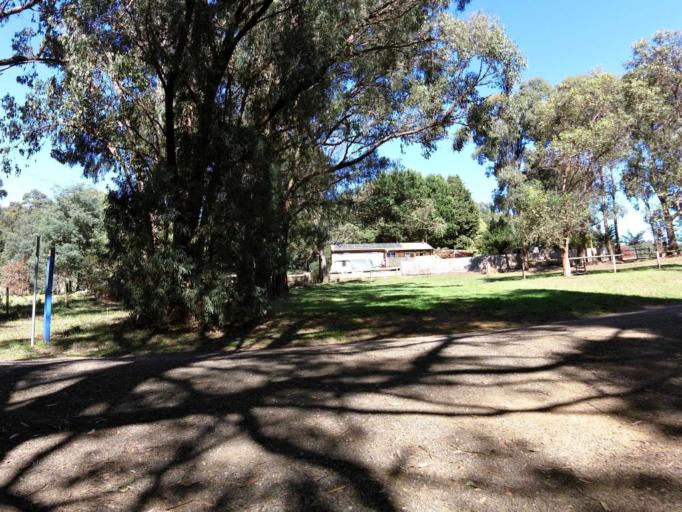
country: AU
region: Victoria
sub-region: Cardinia
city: Cockatoo
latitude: -37.9465
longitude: 145.4975
